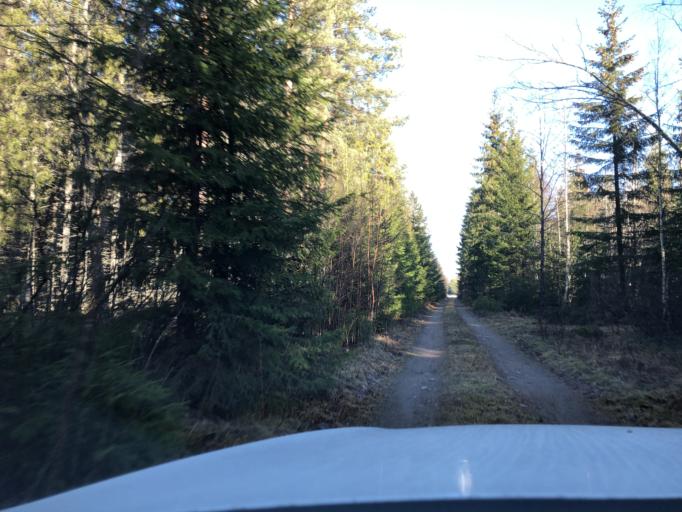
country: SE
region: Gaevleborg
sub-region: Gavle Kommun
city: Hedesunda
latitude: 60.3014
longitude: 16.9016
